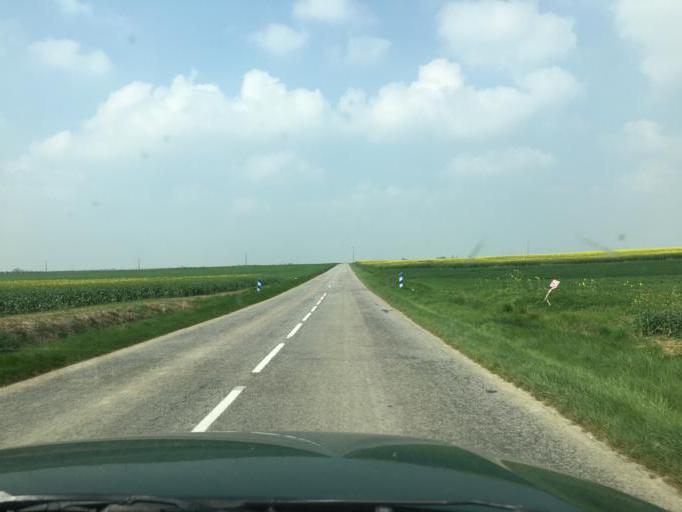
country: FR
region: Centre
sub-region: Departement du Loir-et-Cher
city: Ouzouer-le-Marche
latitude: 47.8338
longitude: 1.5595
